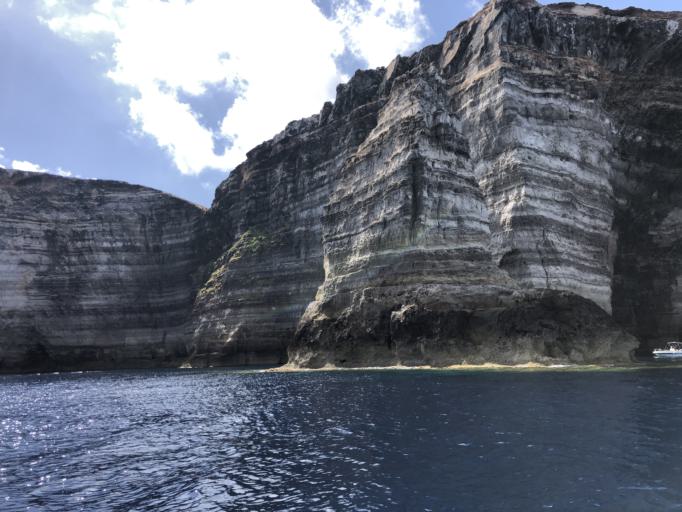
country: IT
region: Sicily
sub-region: Agrigento
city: Lampedusa
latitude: 35.5296
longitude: 12.5277
